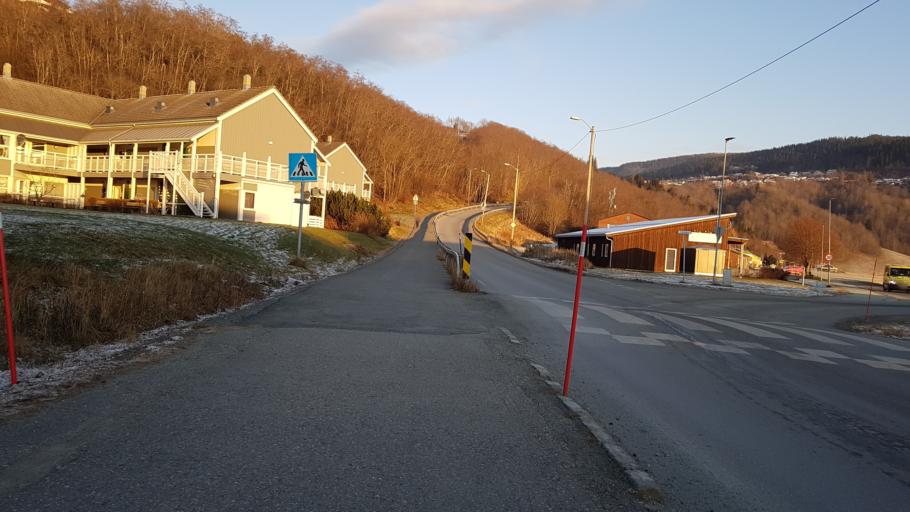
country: NO
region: Sor-Trondelag
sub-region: Melhus
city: Melhus
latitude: 63.2848
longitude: 10.2843
